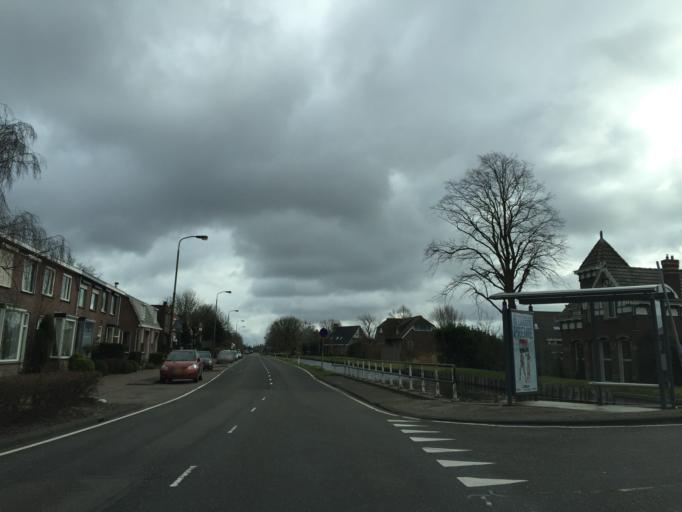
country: NL
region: South Holland
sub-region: Gemeente Lansingerland
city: Berkel en Rodenrijs
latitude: 52.0155
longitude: 4.4844
